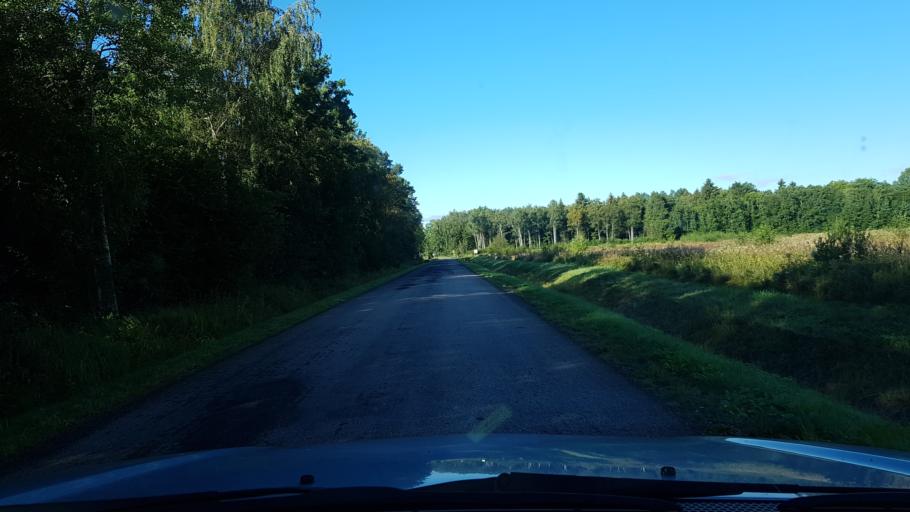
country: EE
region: Harju
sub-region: Rae vald
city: Vaida
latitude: 59.3012
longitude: 24.9197
